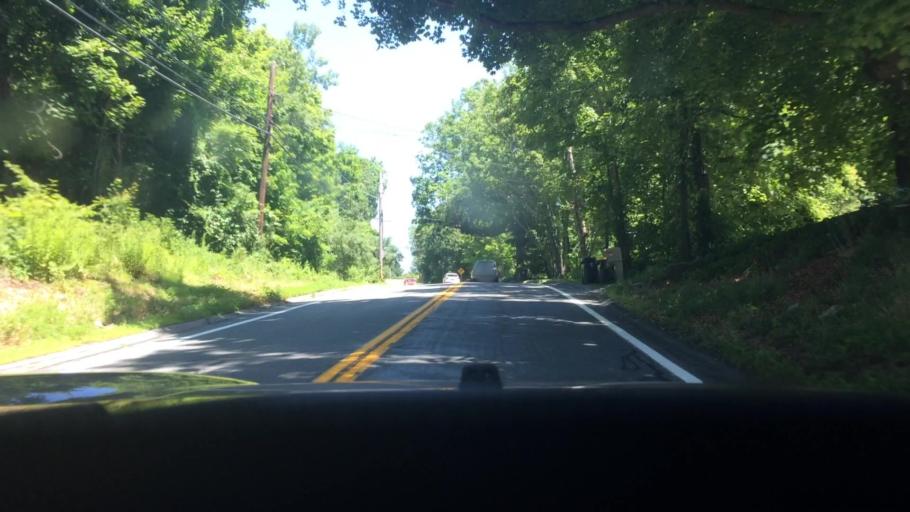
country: US
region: Rhode Island
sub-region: Providence County
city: Harrisville
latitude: 41.9698
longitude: -71.6568
